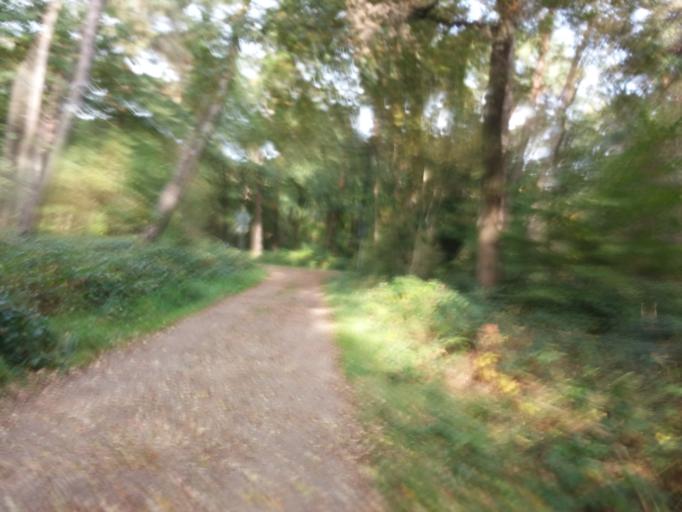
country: DE
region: North Rhine-Westphalia
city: Dorsten
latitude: 51.6548
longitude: 7.0048
